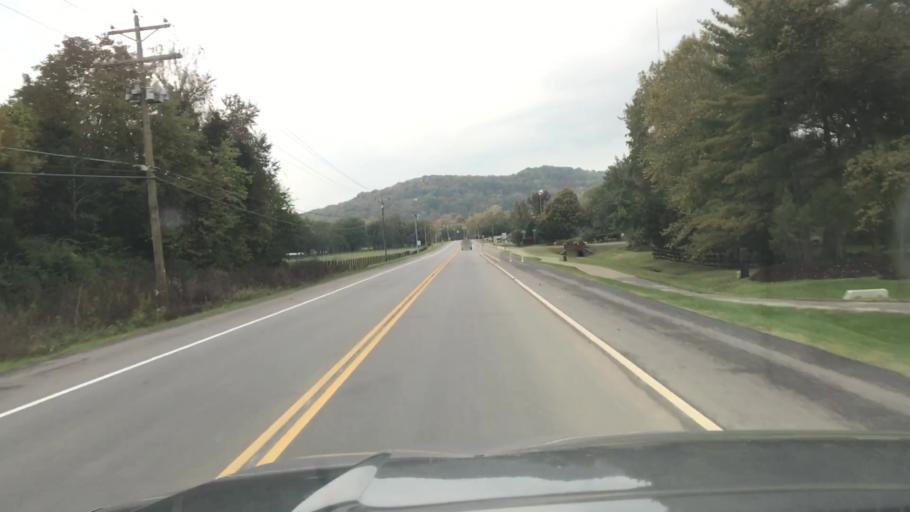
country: US
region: Tennessee
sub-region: Davidson County
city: Forest Hills
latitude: 36.0199
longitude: -86.8475
